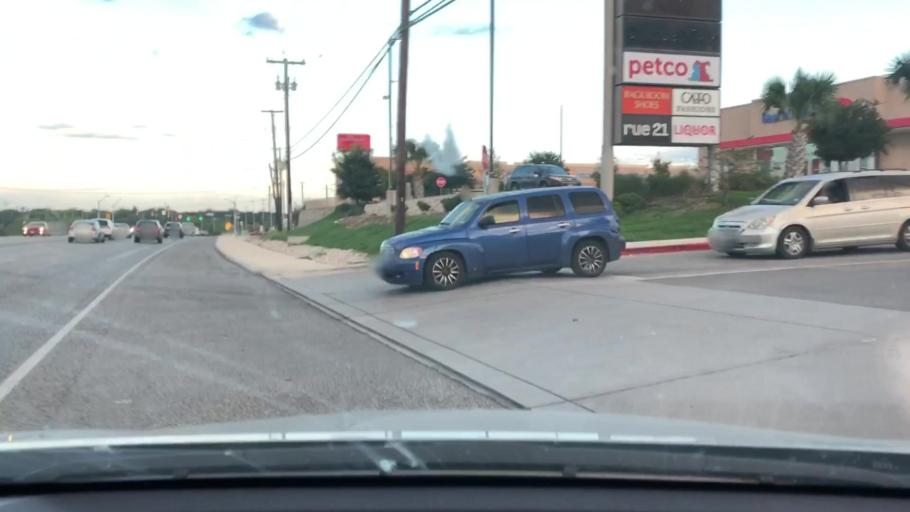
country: US
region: Texas
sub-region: Bexar County
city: Kirby
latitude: 29.4851
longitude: -98.3499
